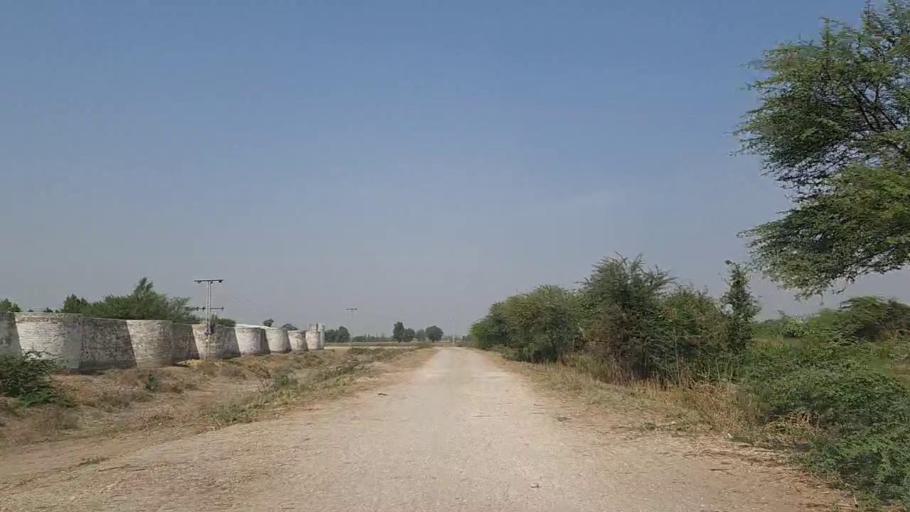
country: PK
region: Sindh
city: Samaro
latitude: 25.2670
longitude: 69.3947
